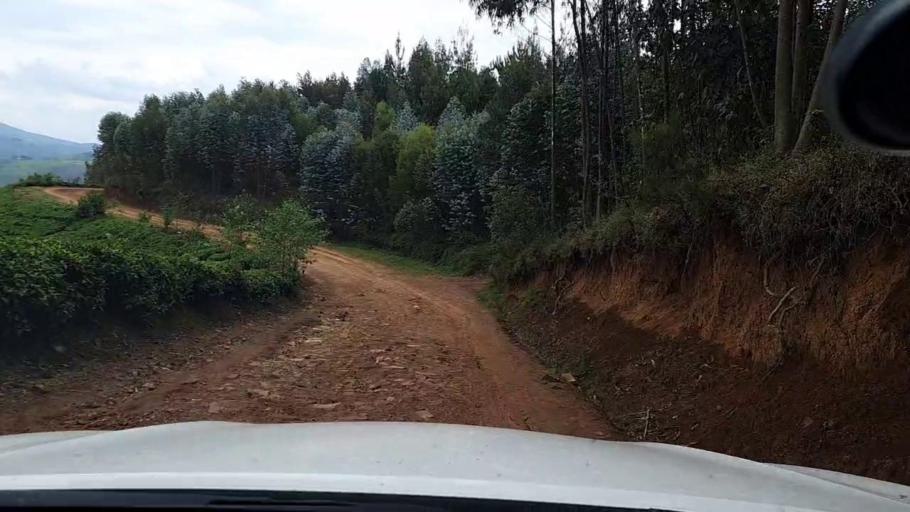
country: RW
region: Western Province
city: Kibuye
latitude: -2.1626
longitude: 29.4533
